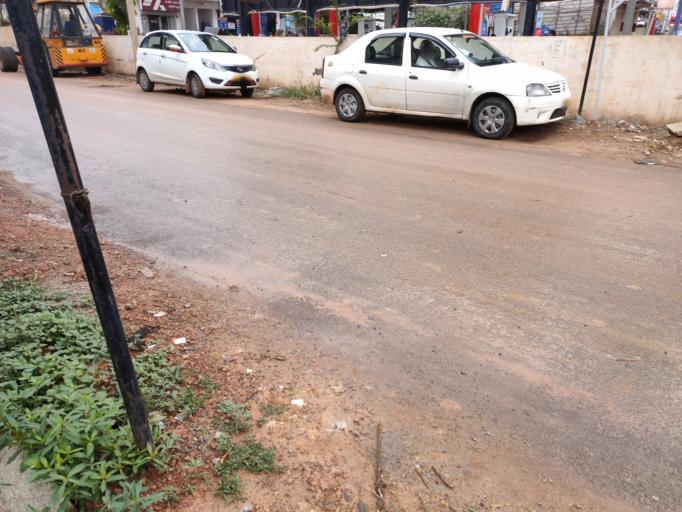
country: IN
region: Karnataka
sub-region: Bangalore Rural
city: Hoskote
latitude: 13.0098
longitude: 77.7593
